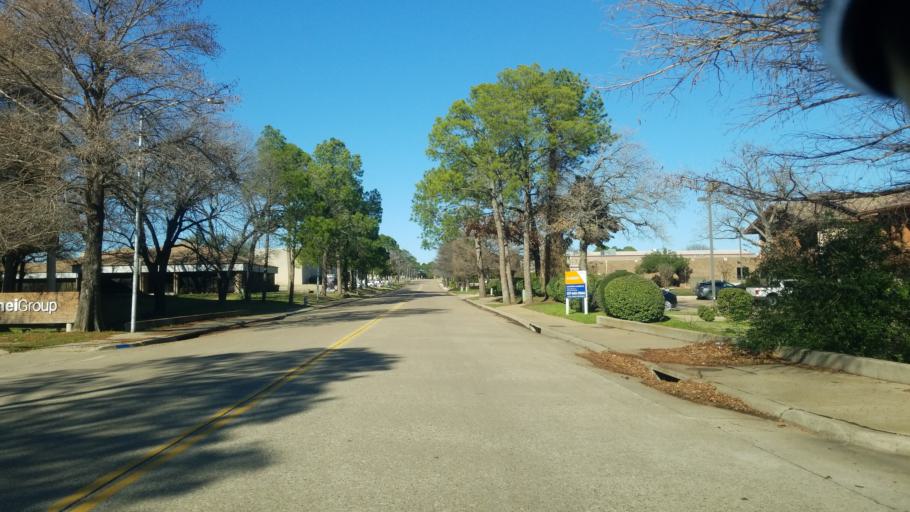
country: US
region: Texas
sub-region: Tarrant County
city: Arlington
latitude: 32.7646
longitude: -97.0679
